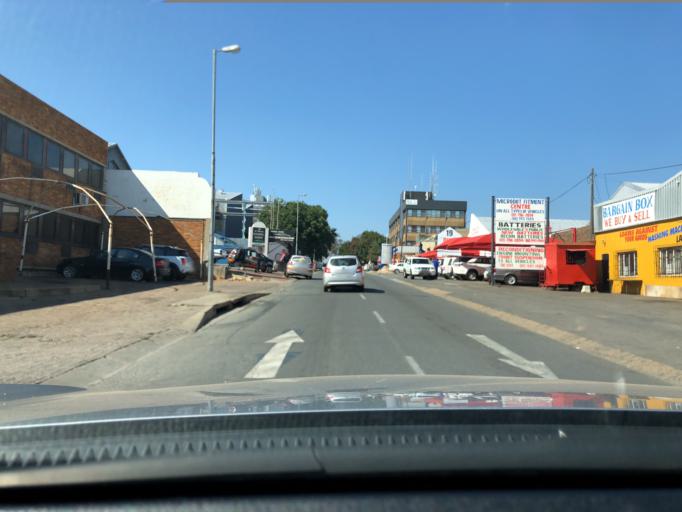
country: ZA
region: Gauteng
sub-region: City of Johannesburg Metropolitan Municipality
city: Modderfontein
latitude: -26.1115
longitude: 28.0831
